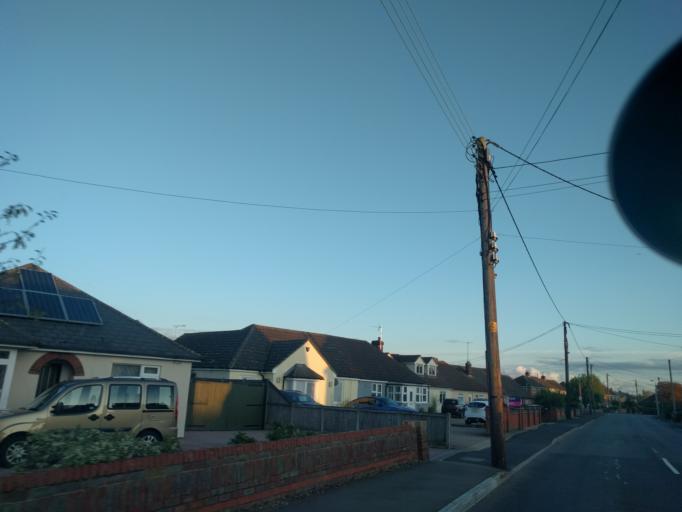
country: GB
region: England
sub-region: Essex
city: Rayne
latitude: 51.8725
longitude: 0.5787
